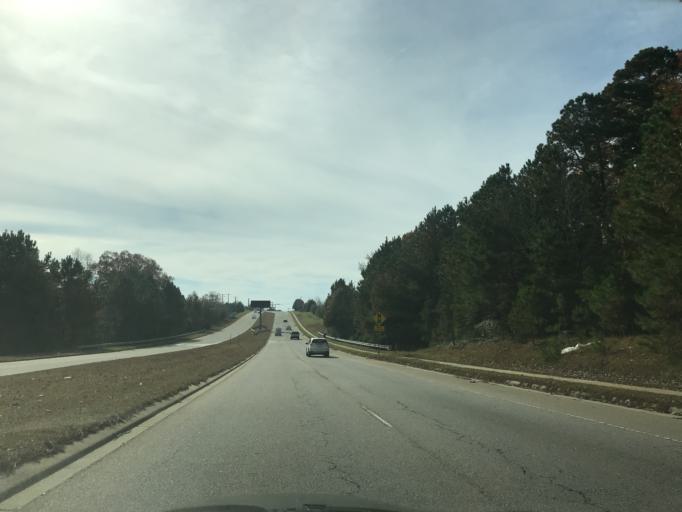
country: US
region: North Carolina
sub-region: Wake County
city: West Raleigh
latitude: 35.8195
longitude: -78.7117
